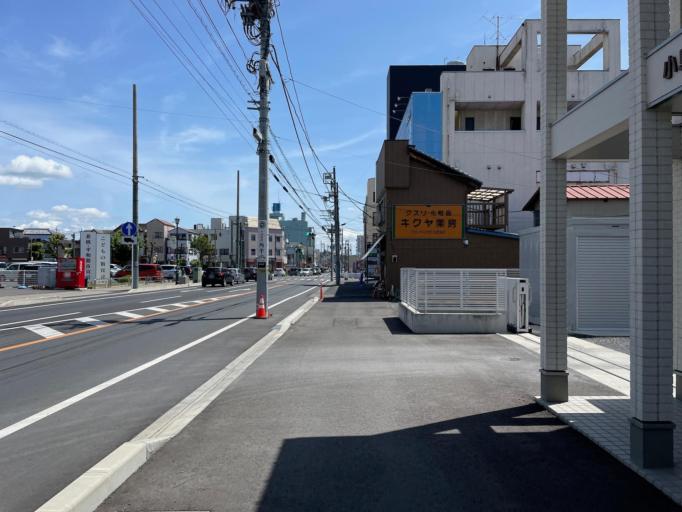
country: JP
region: Tochigi
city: Sano
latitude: 36.3134
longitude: 139.5777
